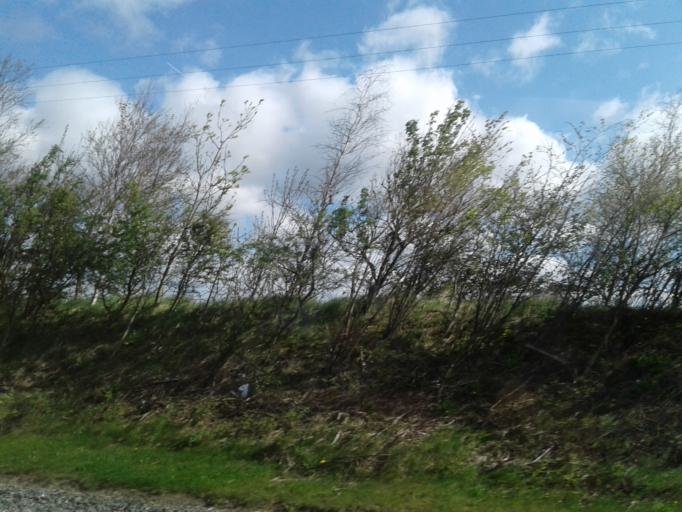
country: IE
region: Leinster
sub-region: An Mhi
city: Ashbourne
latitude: 53.4581
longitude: -6.3550
